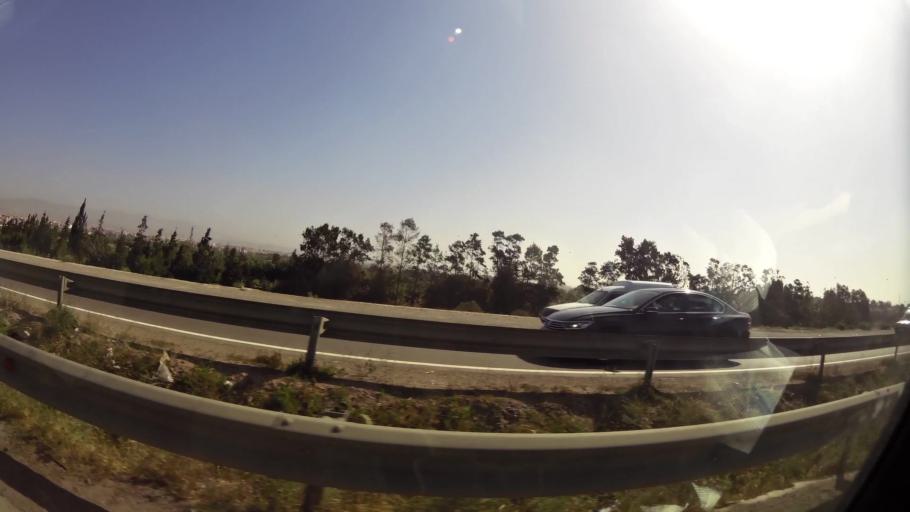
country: MA
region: Souss-Massa-Draa
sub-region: Inezgane-Ait Mellou
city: Inezgane
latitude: 30.3616
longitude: -9.4916
